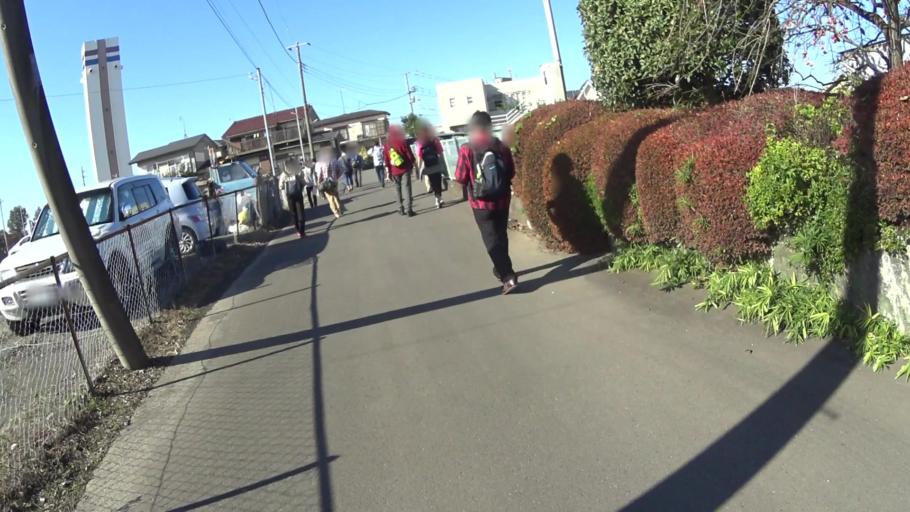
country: JP
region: Tokyo
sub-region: Machida-shi
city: Machida
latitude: 35.5693
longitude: 139.4393
